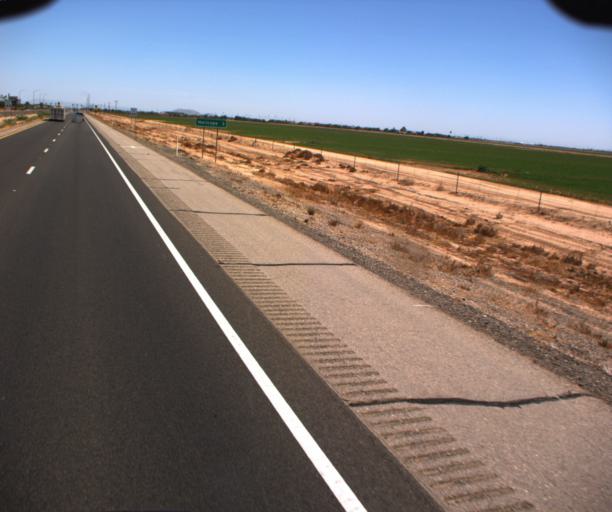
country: US
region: Arizona
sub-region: Pinal County
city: Maricopa
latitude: 33.0192
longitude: -112.0478
